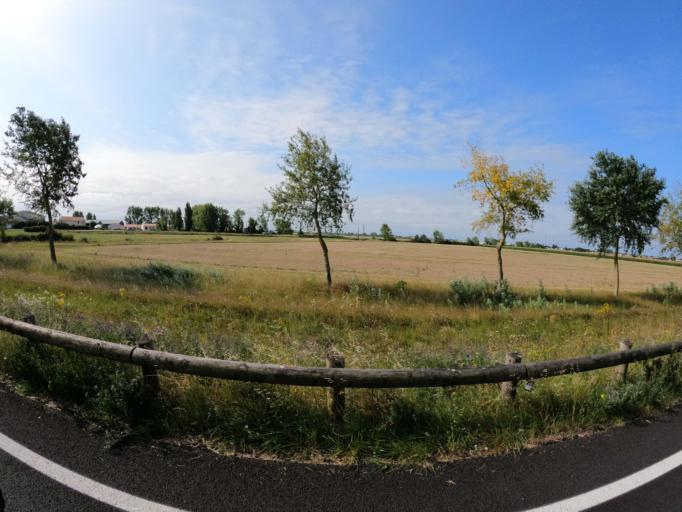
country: FR
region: Pays de la Loire
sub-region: Departement de la Vendee
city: Triaize
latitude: 46.3388
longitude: -1.2835
